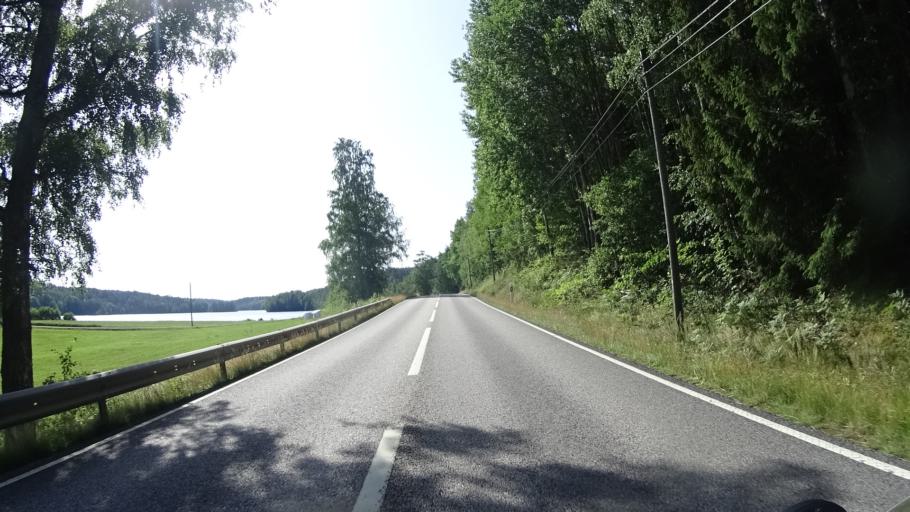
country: SE
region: Kalmar
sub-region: Vasterviks Kommun
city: Overum
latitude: 58.0047
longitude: 16.2726
